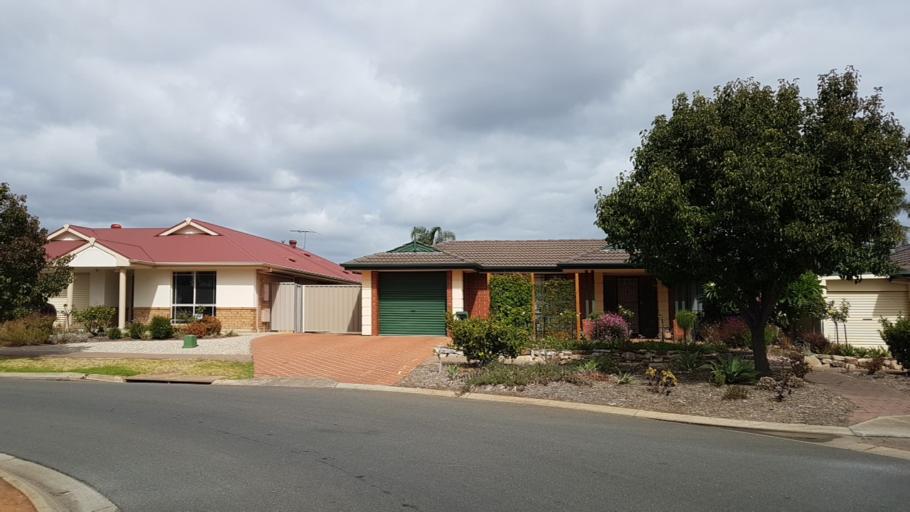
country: AU
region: South Australia
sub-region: Marion
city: Clovelly Park
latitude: -35.0006
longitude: 138.5718
